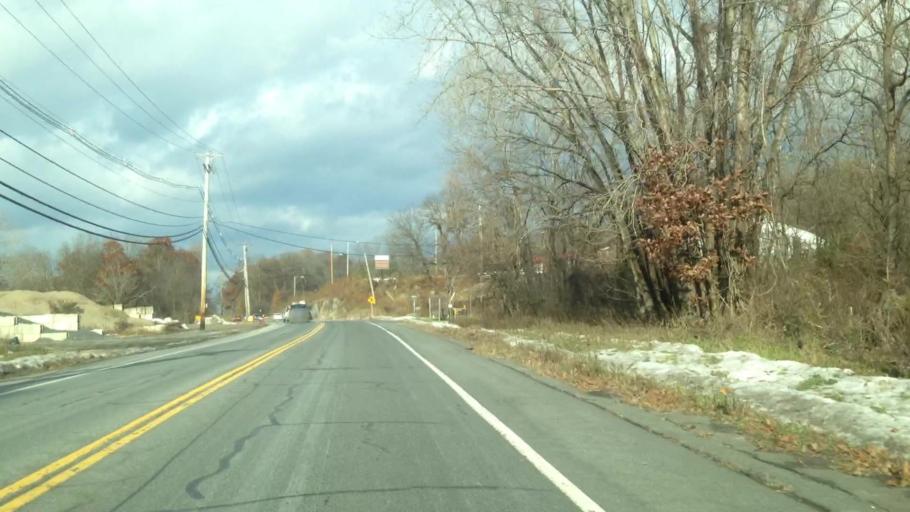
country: US
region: New York
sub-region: Ulster County
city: Lincoln Park
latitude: 41.9479
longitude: -73.9910
